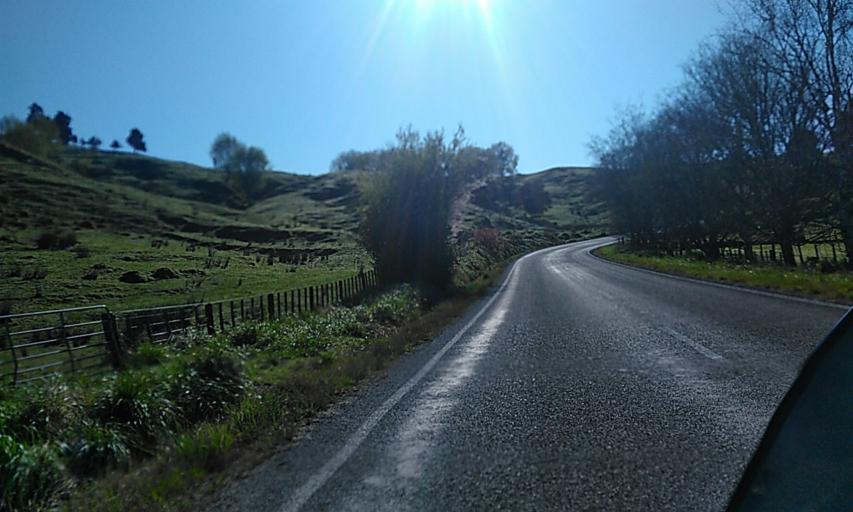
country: NZ
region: Gisborne
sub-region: Gisborne District
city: Gisborne
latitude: -38.5049
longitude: 178.0473
